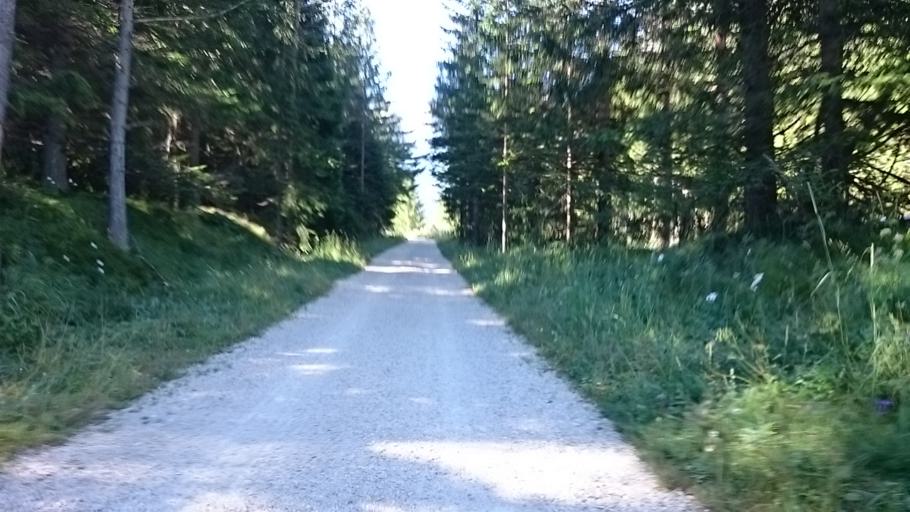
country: IT
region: Trentino-Alto Adige
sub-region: Bolzano
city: Dobbiaco
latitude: 46.6447
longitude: 12.2327
